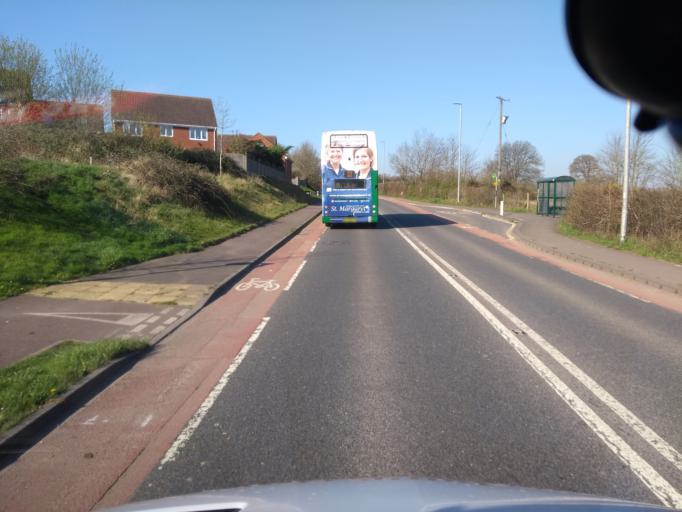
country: GB
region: England
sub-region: Somerset
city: Bishops Lydeard
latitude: 50.9853
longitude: -3.2191
